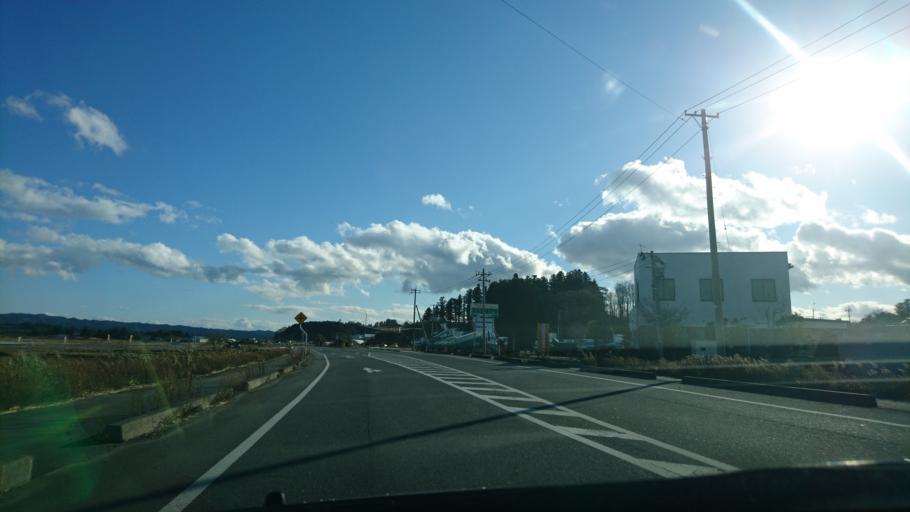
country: JP
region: Iwate
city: Ichinoseki
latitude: 38.7413
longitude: 141.2555
